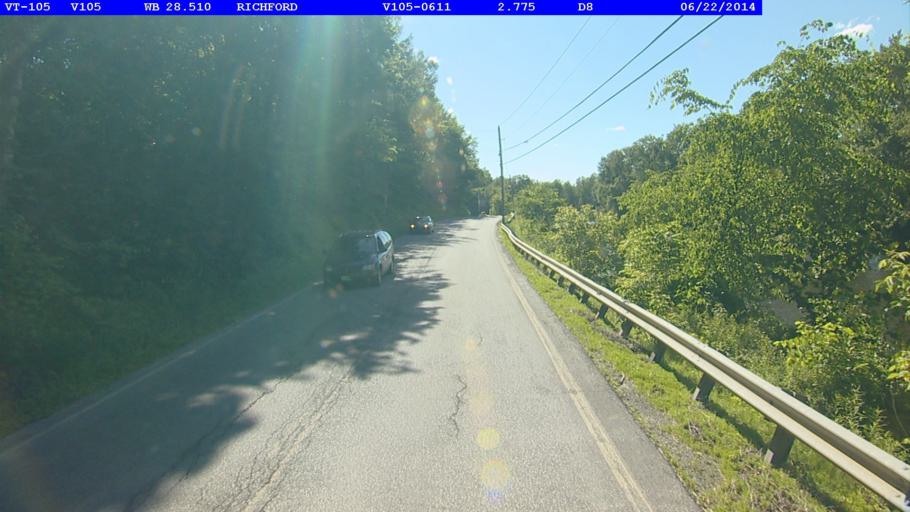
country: US
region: Vermont
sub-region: Franklin County
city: Richford
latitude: 44.9848
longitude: -72.6625
